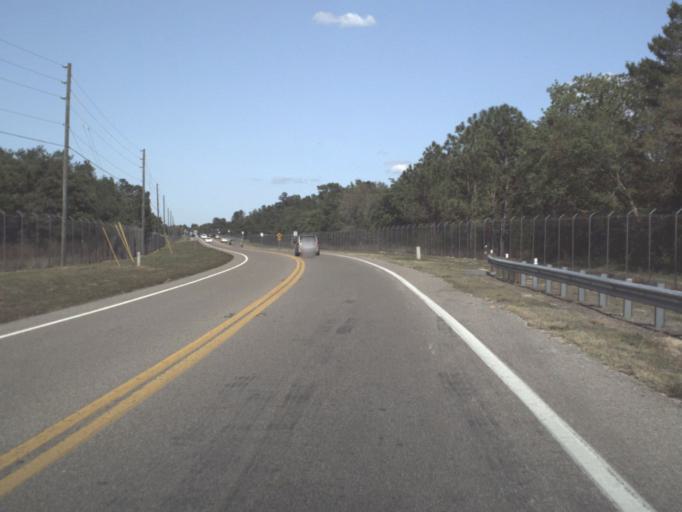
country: US
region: Florida
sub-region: Lake County
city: Mount Plymouth
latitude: 28.8129
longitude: -81.5020
